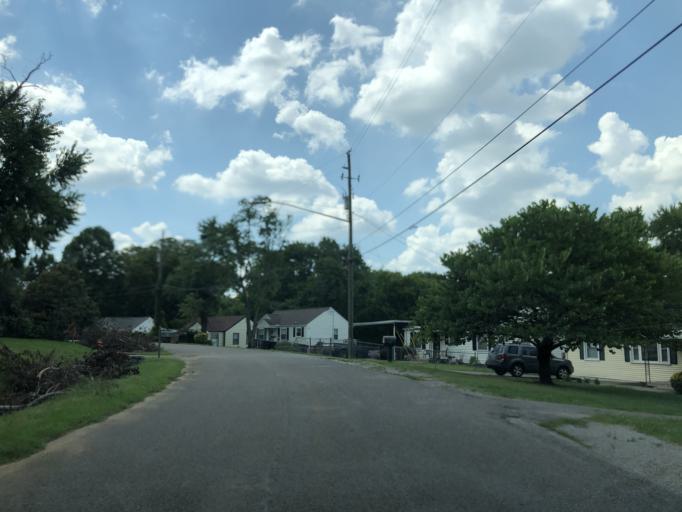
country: US
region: Tennessee
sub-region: Davidson County
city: Oak Hill
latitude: 36.1216
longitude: -86.7357
